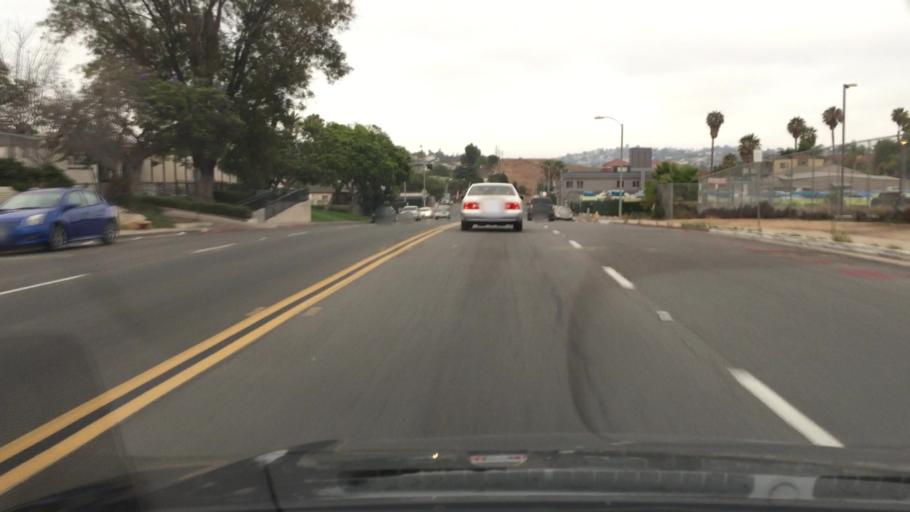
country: US
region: California
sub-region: San Diego County
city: National City
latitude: 32.7114
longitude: -117.0966
